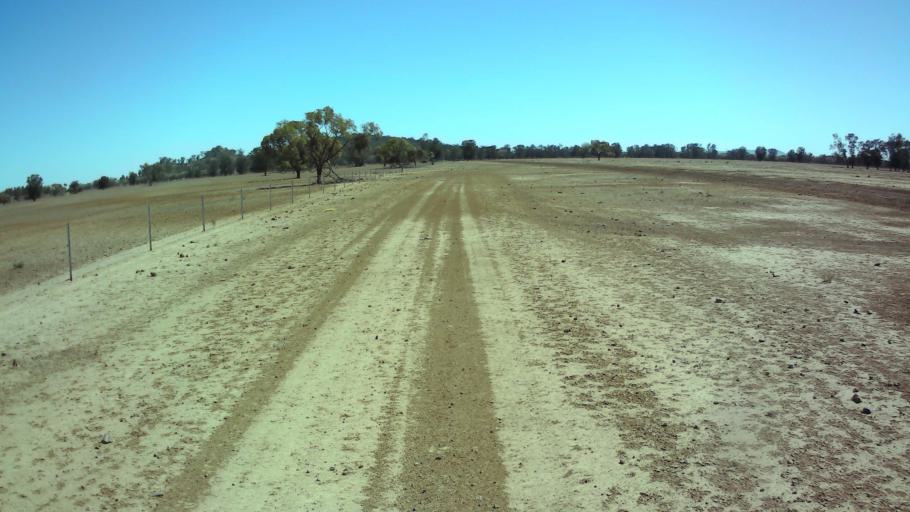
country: AU
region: New South Wales
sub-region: Bland
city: West Wyalong
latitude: -33.7490
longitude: 147.6602
